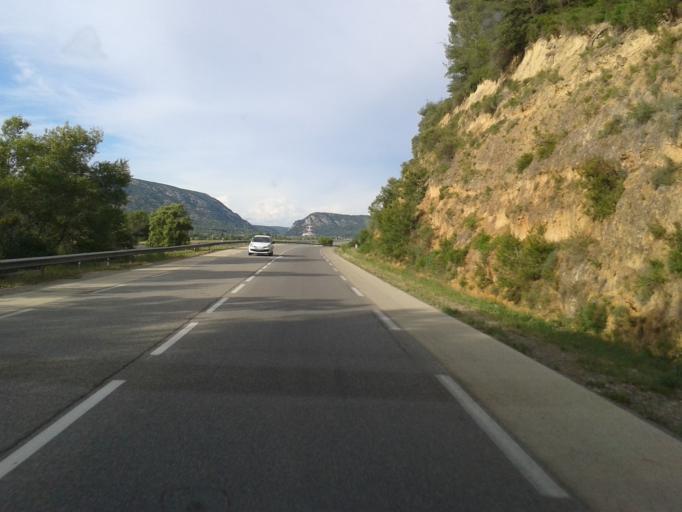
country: FR
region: Provence-Alpes-Cote d'Azur
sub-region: Departement des Bouches-du-Rhone
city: Peyrolles-en-Provence
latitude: 43.6527
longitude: 5.6107
